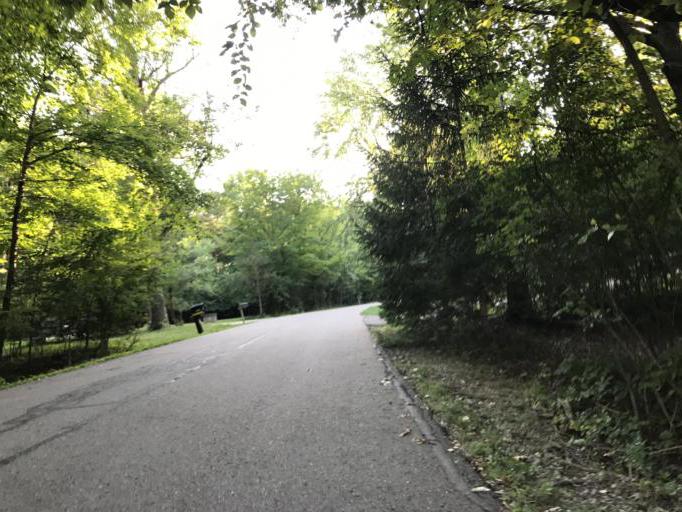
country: US
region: Michigan
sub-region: Oakland County
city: Farmington Hills
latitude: 42.4783
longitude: -83.3465
